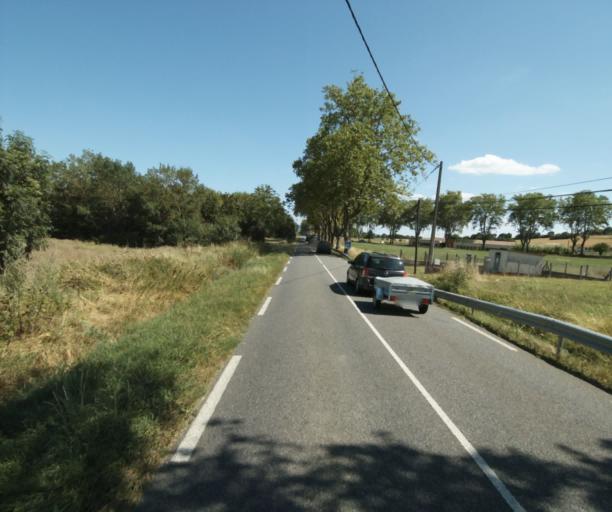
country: FR
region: Midi-Pyrenees
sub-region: Departement de la Haute-Garonne
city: Saint-Felix-Lauragais
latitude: 43.4909
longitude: 1.9033
